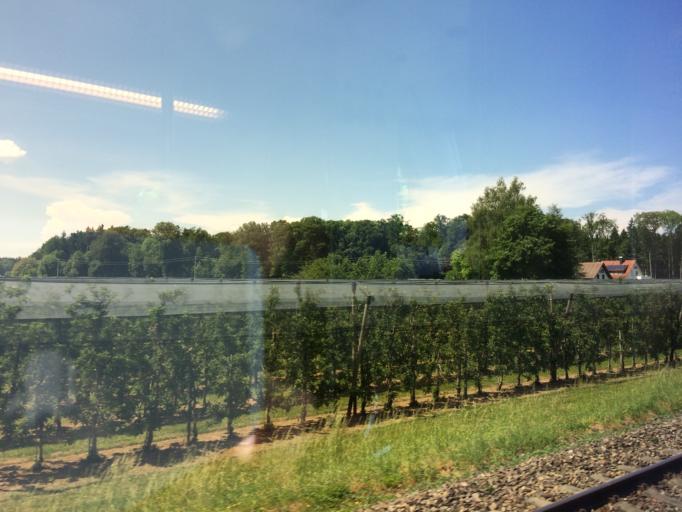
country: DE
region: Baden-Wuerttemberg
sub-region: Tuebingen Region
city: Meckenbeuren
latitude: 47.7087
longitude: 9.5629
